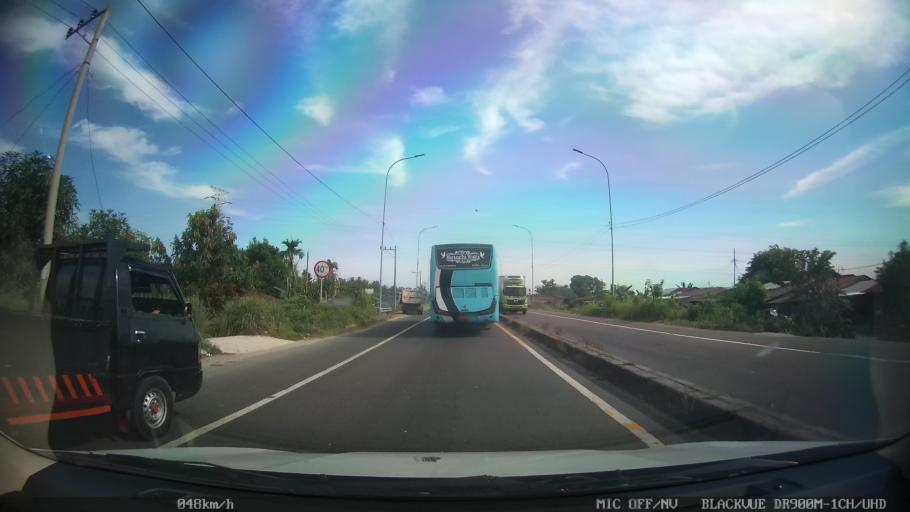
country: ID
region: North Sumatra
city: Sunggal
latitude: 3.6174
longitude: 98.6293
